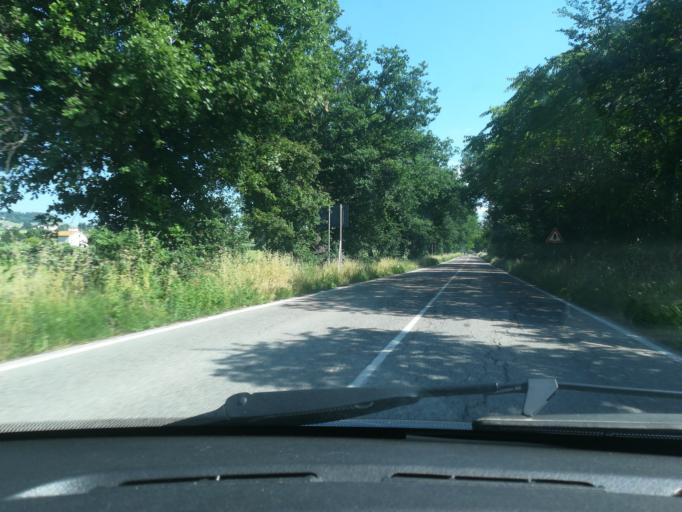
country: IT
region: The Marches
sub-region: Provincia di Macerata
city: Pollenza
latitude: 43.2927
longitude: 13.3790
